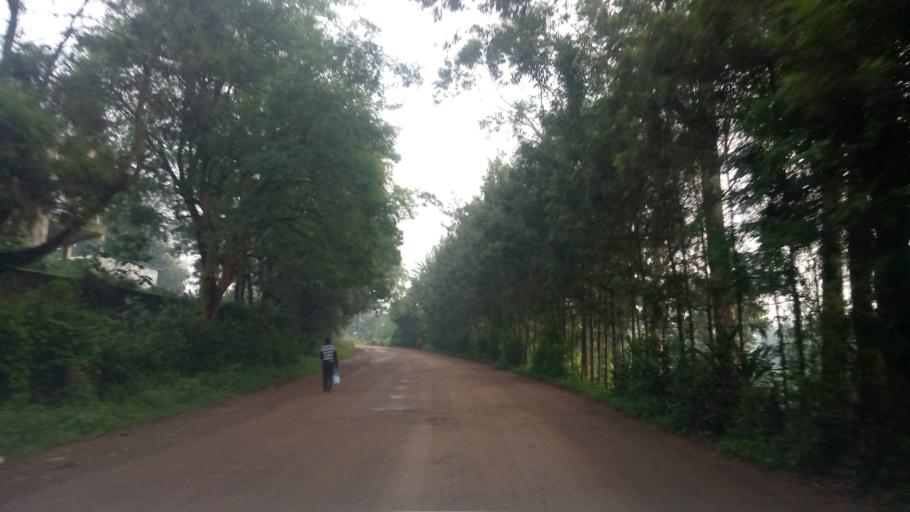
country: ET
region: Oromiya
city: Jima
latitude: 7.6858
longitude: 36.8320
